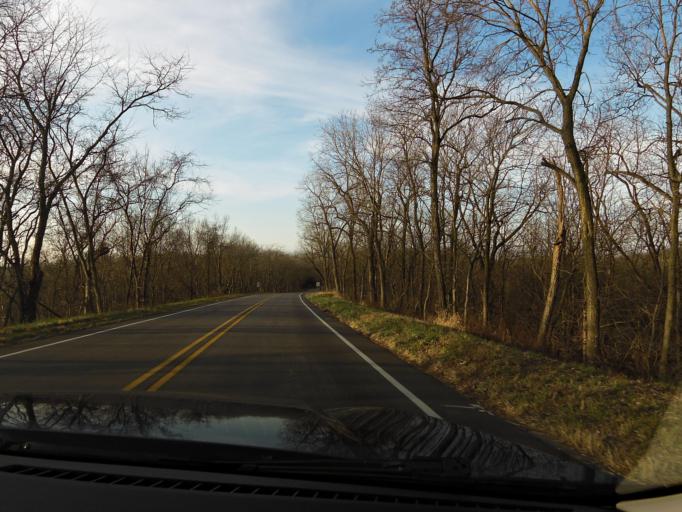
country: US
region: Illinois
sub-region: Bond County
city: Greenville
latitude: 38.9228
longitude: -89.2536
